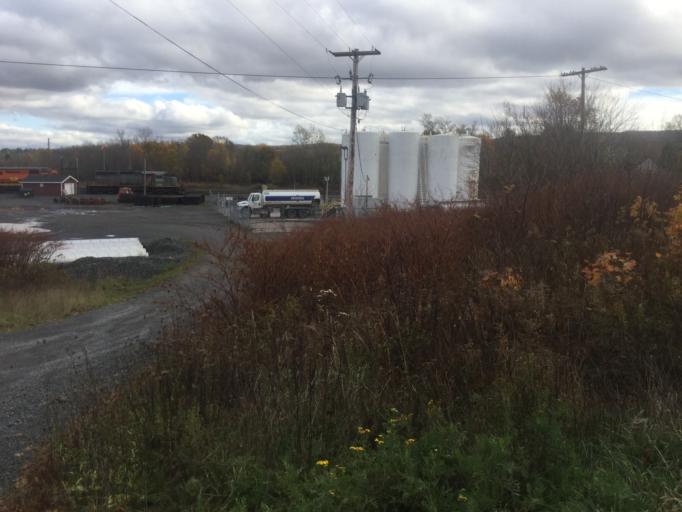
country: CA
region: Nova Scotia
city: New Glasgow
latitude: 45.5548
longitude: -62.6611
